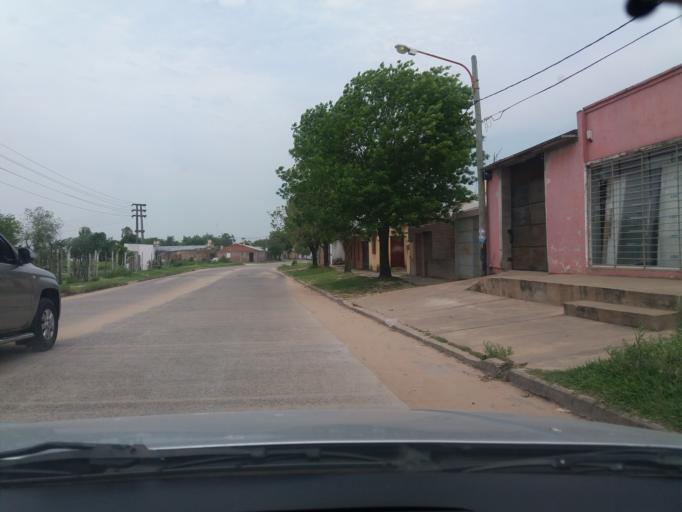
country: AR
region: Corrientes
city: Corrientes
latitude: -27.5102
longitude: -58.7985
